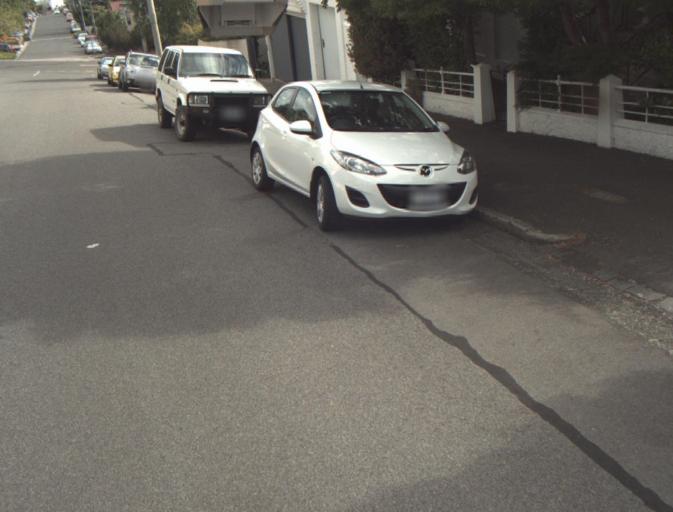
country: AU
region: Tasmania
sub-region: Launceston
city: East Launceston
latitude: -41.4359
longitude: 147.1500
